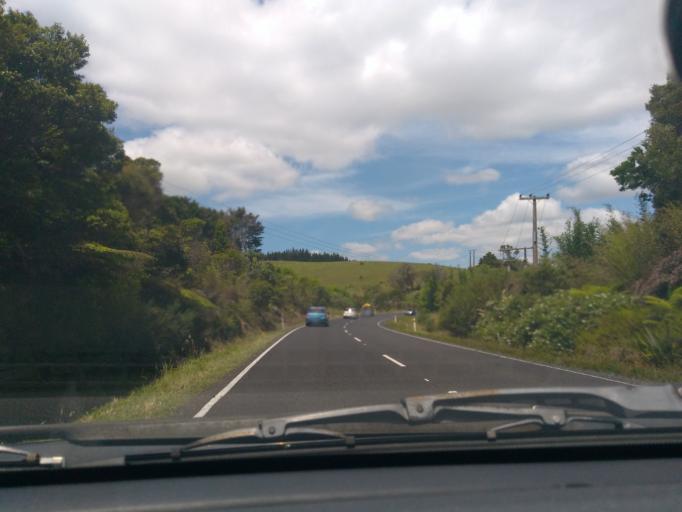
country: NZ
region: Northland
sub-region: Far North District
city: Kerikeri
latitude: -35.1513
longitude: 173.8873
